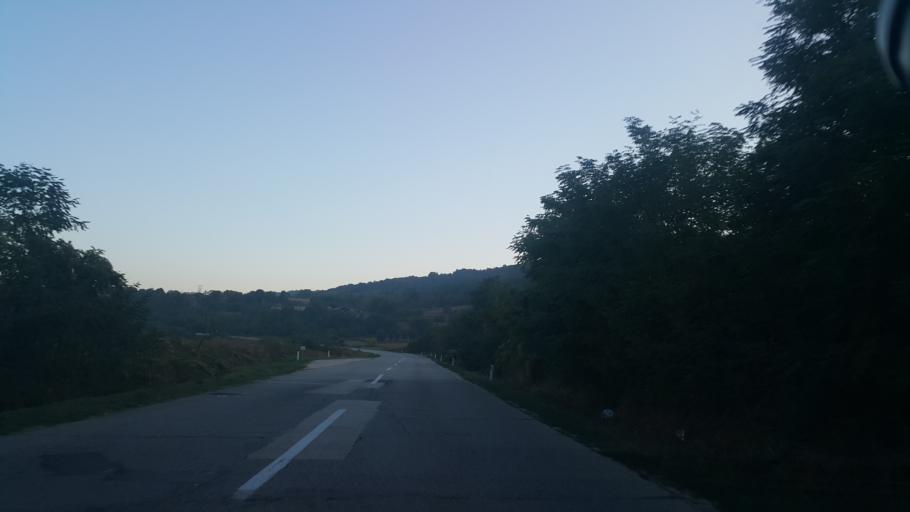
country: RS
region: Central Serbia
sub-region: Zajecarski Okrug
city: Zajecar
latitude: 43.7465
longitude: 22.3127
